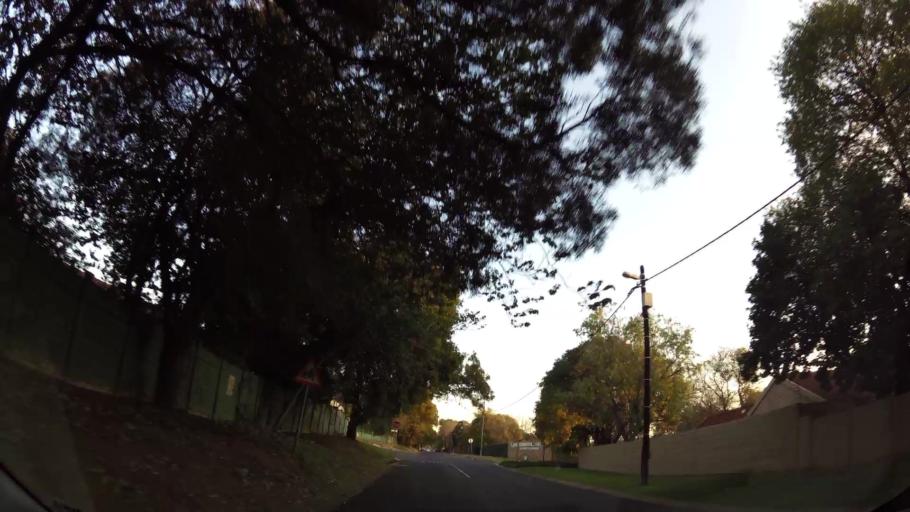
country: ZA
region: Gauteng
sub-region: City of Johannesburg Metropolitan Municipality
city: Johannesburg
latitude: -26.1138
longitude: 27.9953
